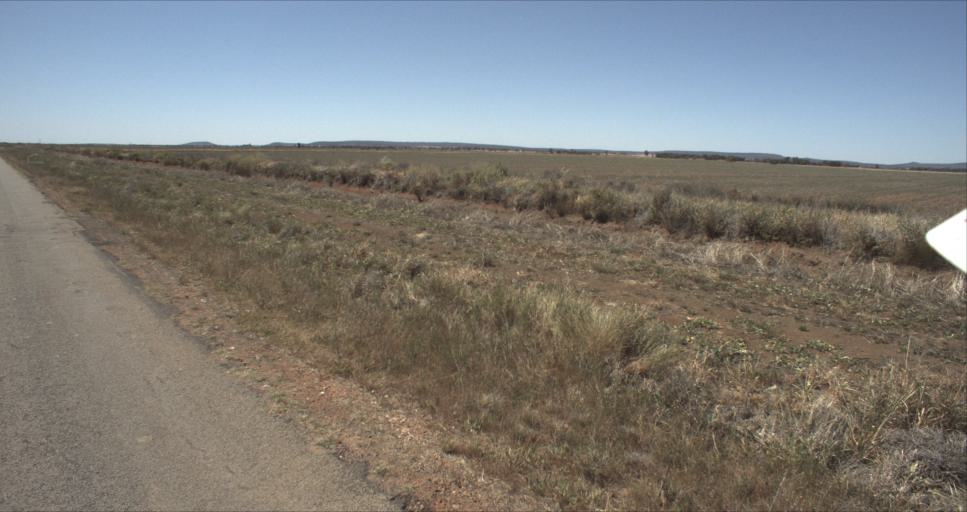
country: AU
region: New South Wales
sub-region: Leeton
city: Leeton
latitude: -34.5038
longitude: 146.3443
